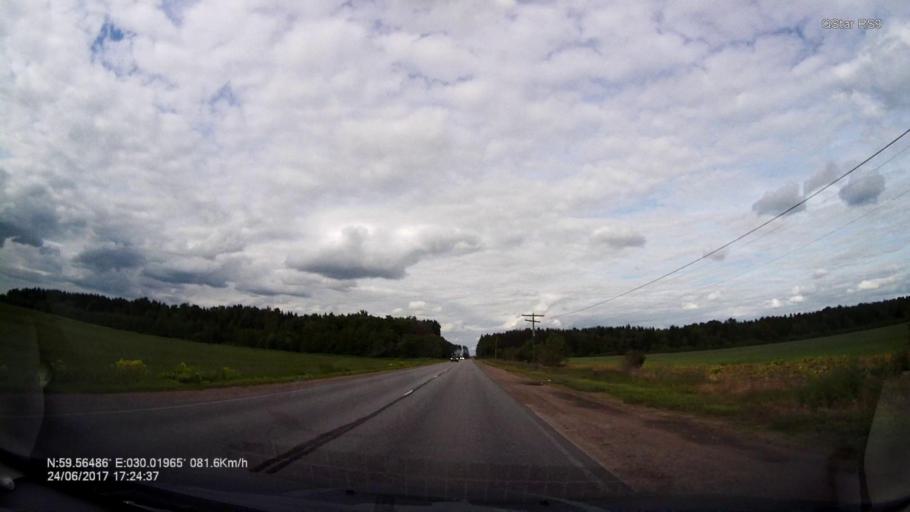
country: RU
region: Leningrad
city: Mariyenburg
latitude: 59.5650
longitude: 30.0200
